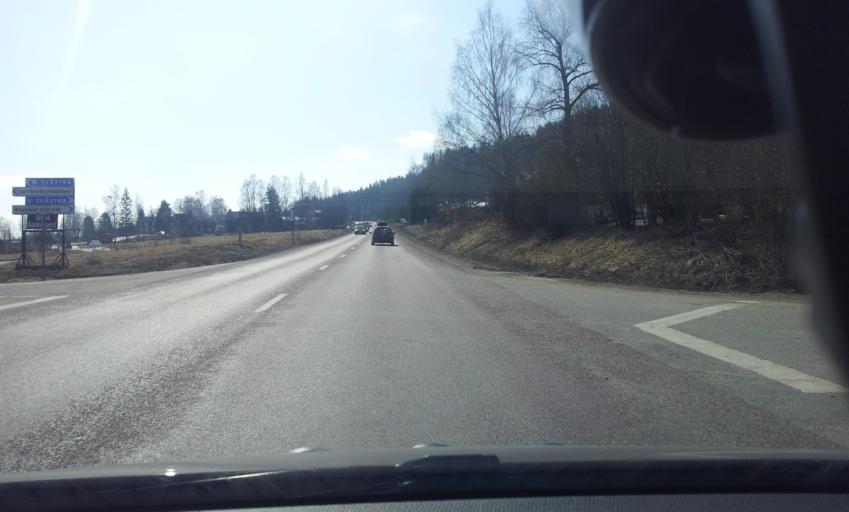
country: SE
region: Gaevleborg
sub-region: Ljusdals Kommun
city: Jaervsoe
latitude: 61.7476
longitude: 16.1595
